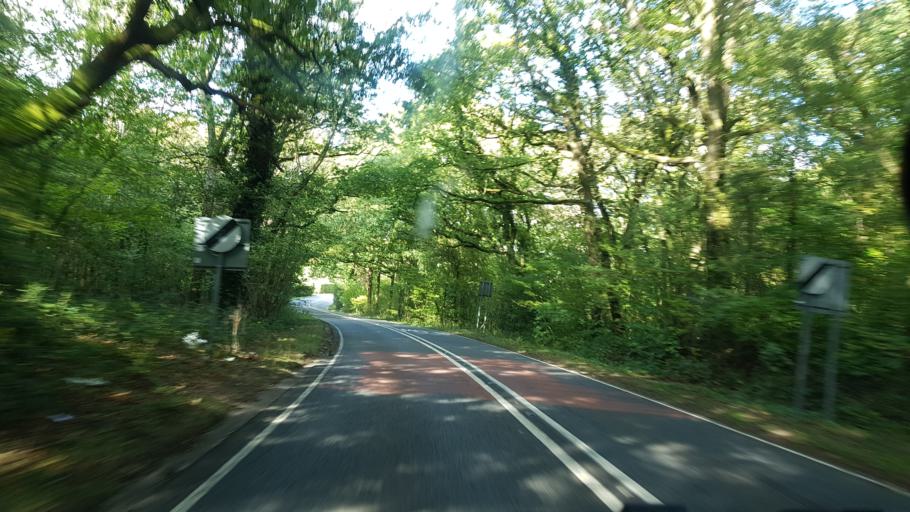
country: GB
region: England
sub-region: Surrey
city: Chiddingfold
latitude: 51.0642
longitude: -0.6438
